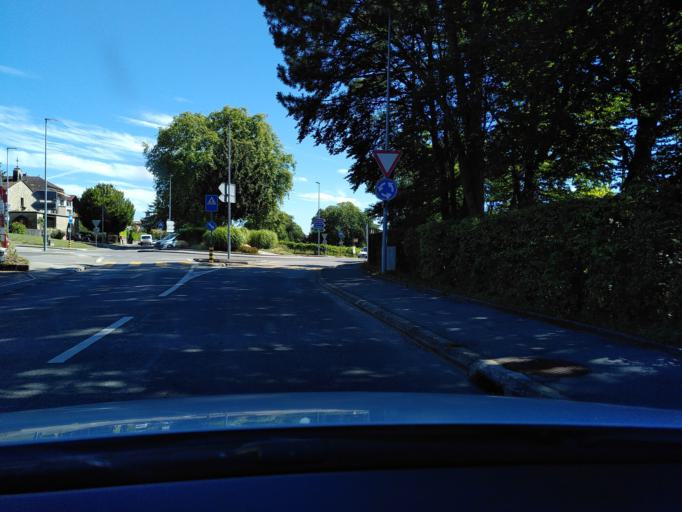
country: CH
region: Vaud
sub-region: Morges District
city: Aubonne
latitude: 46.4923
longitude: 6.3892
